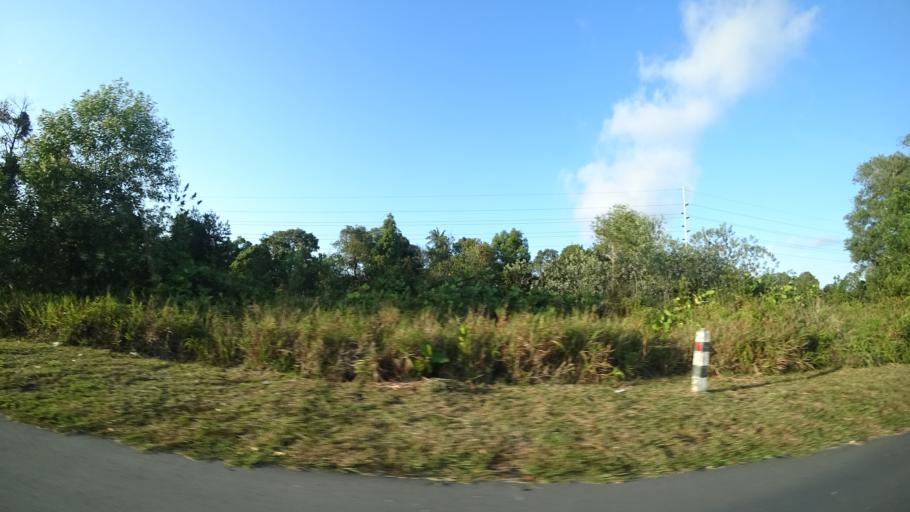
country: BN
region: Tutong
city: Tutong
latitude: 4.7331
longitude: 114.5701
